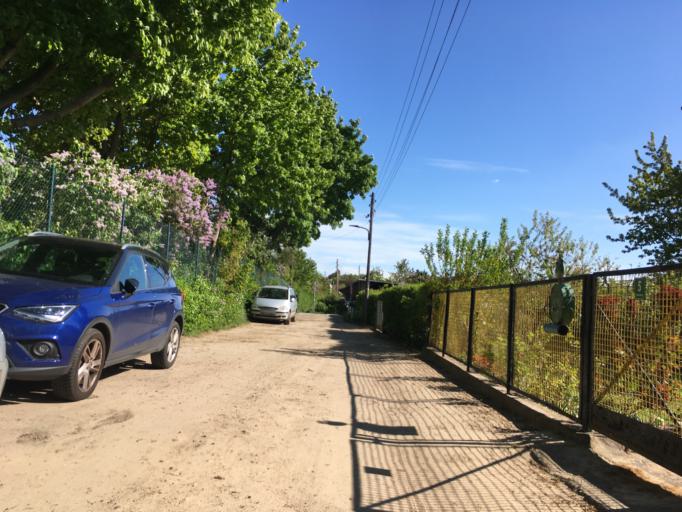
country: DE
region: Berlin
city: Niederschonhausen
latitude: 52.6004
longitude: 13.3989
